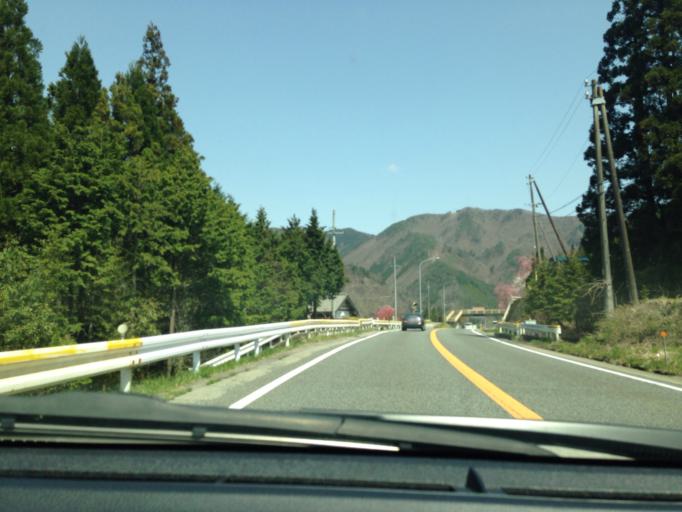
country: JP
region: Gifu
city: Takayama
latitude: 35.9596
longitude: 137.2602
